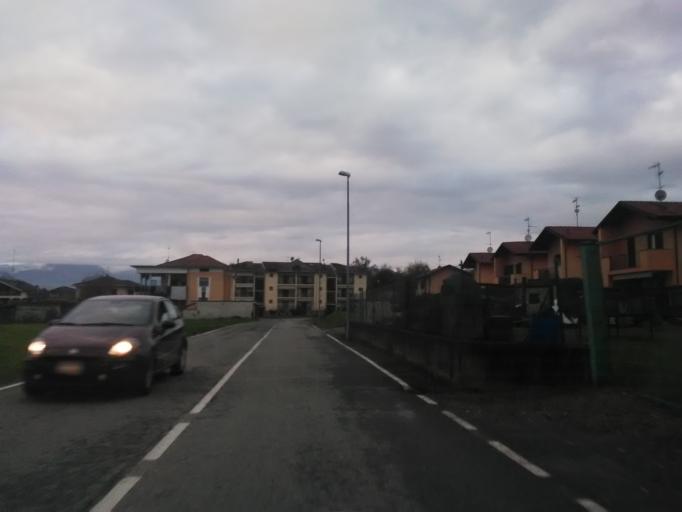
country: IT
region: Piedmont
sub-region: Provincia di Novara
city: Prato Sesia
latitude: 45.6529
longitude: 8.3746
